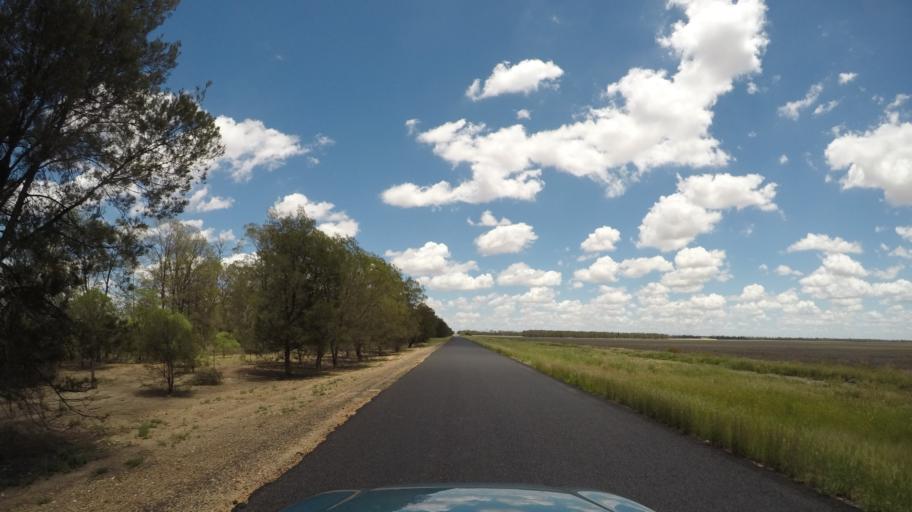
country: AU
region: Queensland
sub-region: Goondiwindi
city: Goondiwindi
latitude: -28.1709
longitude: 150.2175
